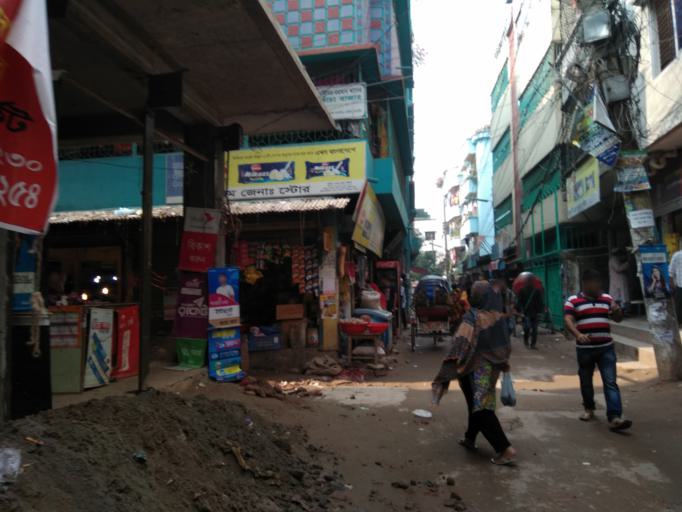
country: BD
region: Dhaka
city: Tungi
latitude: 23.8597
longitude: 90.3884
